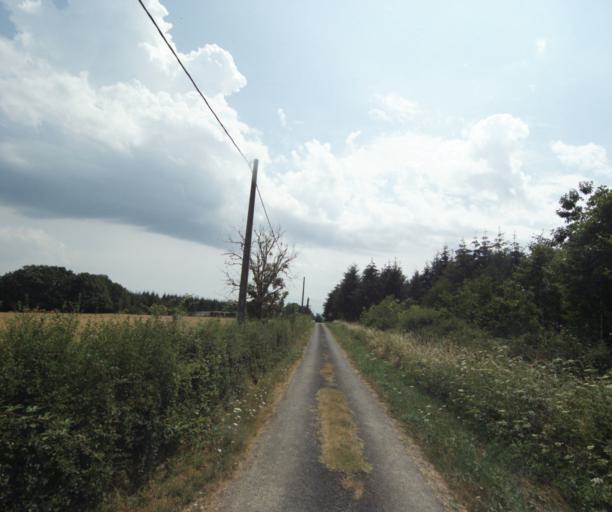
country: FR
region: Bourgogne
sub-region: Departement de Saone-et-Loire
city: Gueugnon
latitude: 46.6058
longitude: 4.0168
